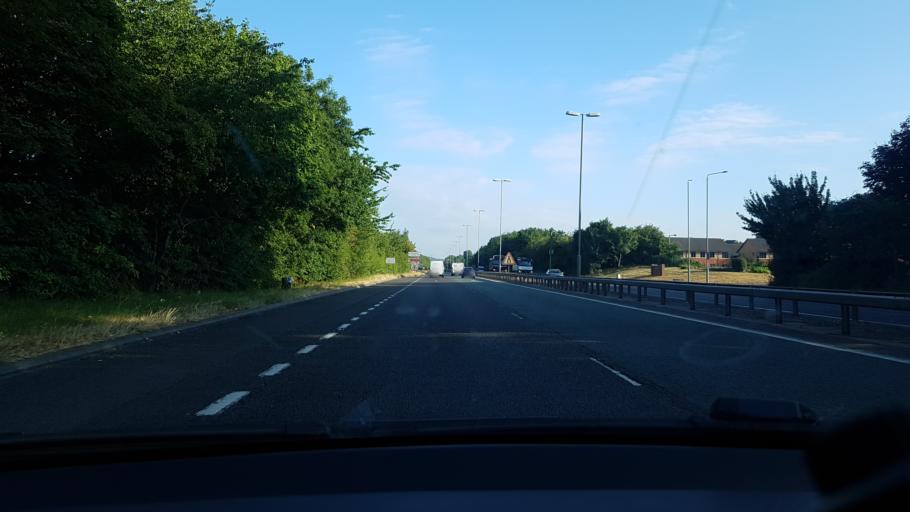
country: GB
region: England
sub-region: Nottinghamshire
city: Eastwood
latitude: 53.0121
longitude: -1.3151
